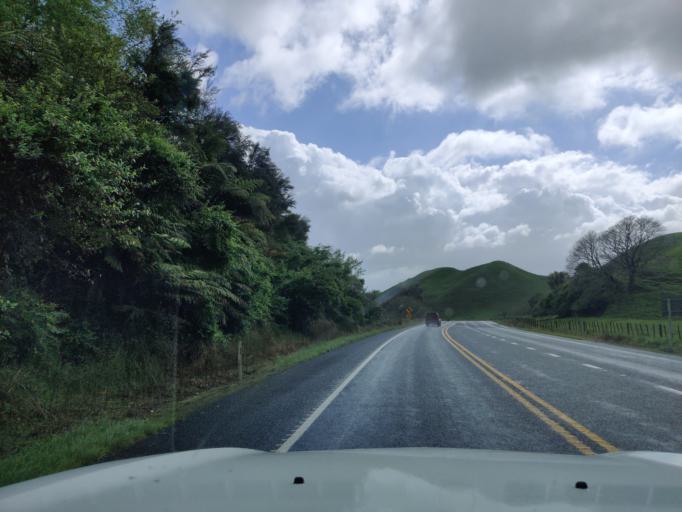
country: NZ
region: Waikato
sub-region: Matamata-Piako District
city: Matamata
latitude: -37.9783
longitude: 175.7396
